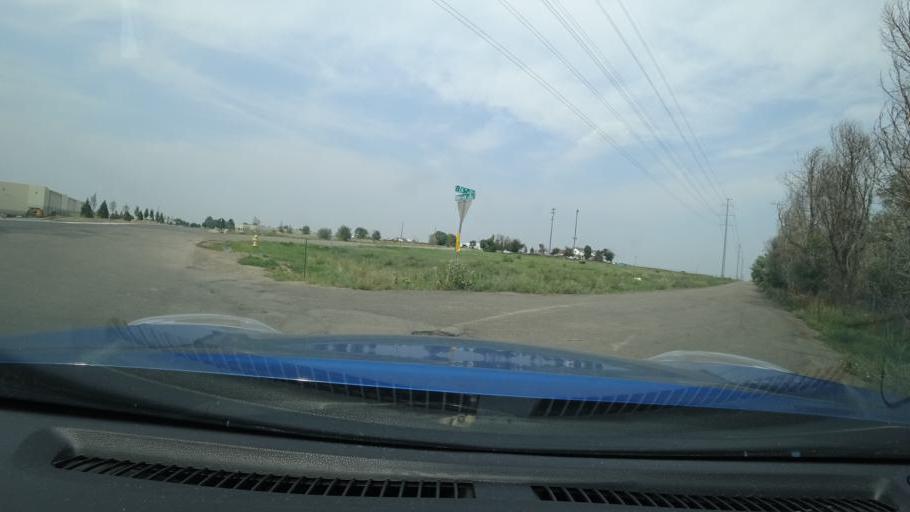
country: US
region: Colorado
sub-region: Adams County
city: Aurora
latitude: 39.7546
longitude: -104.7536
